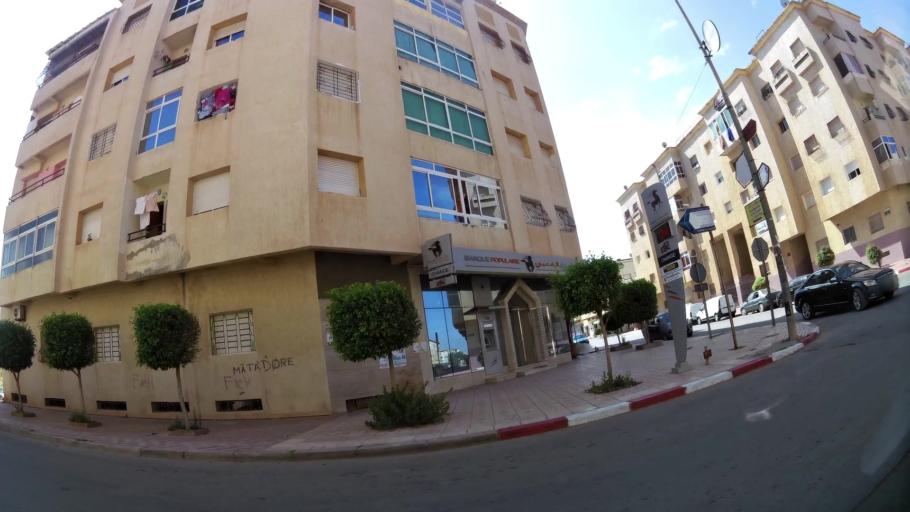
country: MA
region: Rabat-Sale-Zemmour-Zaer
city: Sale
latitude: 34.0798
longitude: -6.7883
